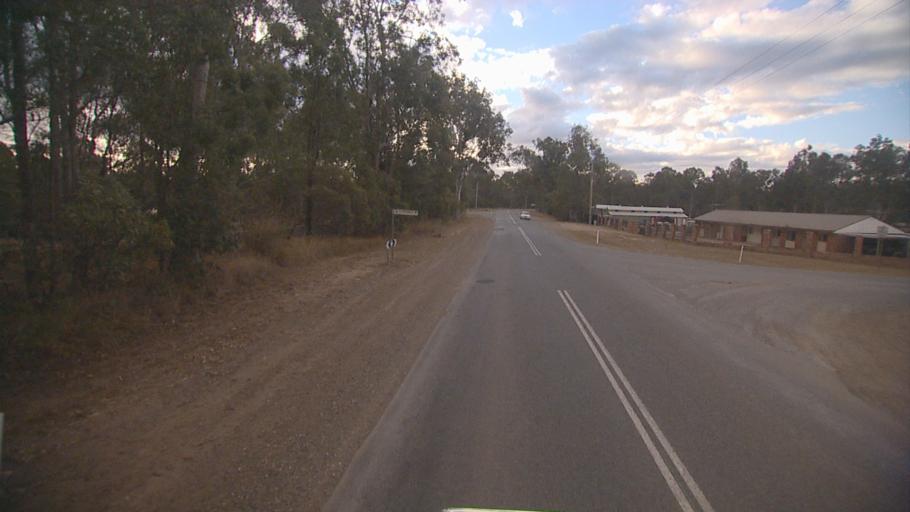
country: AU
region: Queensland
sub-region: Logan
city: Cedar Vale
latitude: -27.8550
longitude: 153.0530
